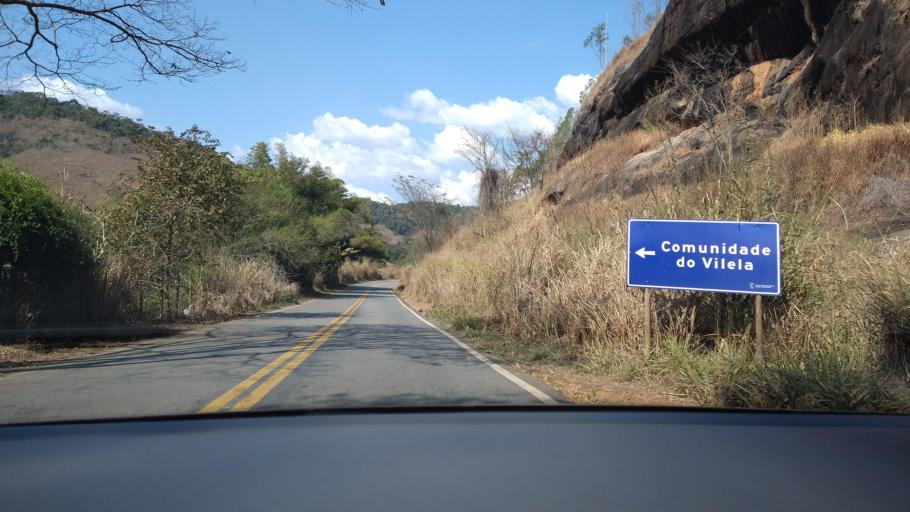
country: BR
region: Minas Gerais
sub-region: Rio Piracicaba
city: Rio Piracicaba
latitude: -19.9551
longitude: -43.1638
